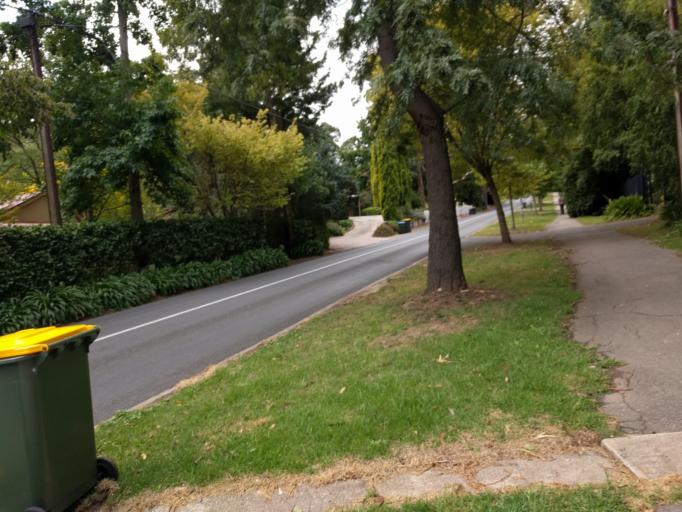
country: AU
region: South Australia
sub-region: Adelaide Hills
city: Heathfield
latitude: -35.0005
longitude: 138.7244
